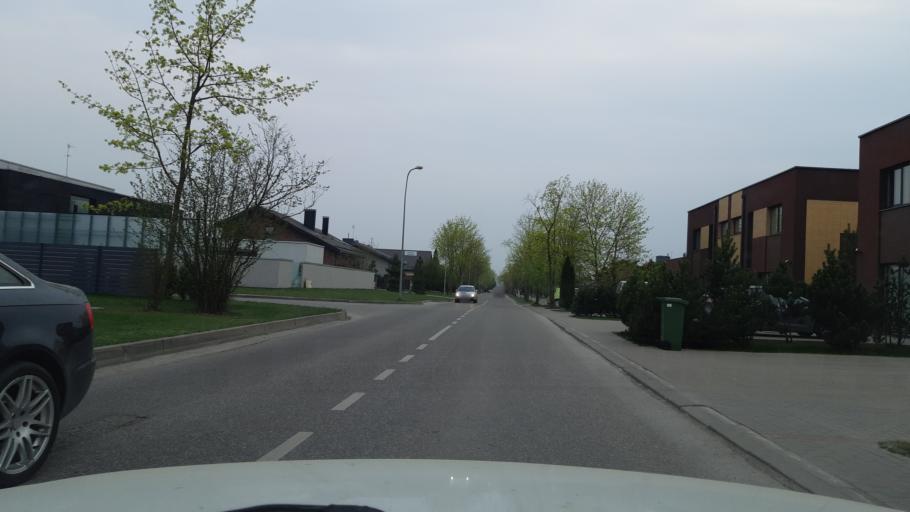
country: LT
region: Kauno apskritis
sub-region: Kaunas
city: Sargenai
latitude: 54.9451
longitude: 23.9045
